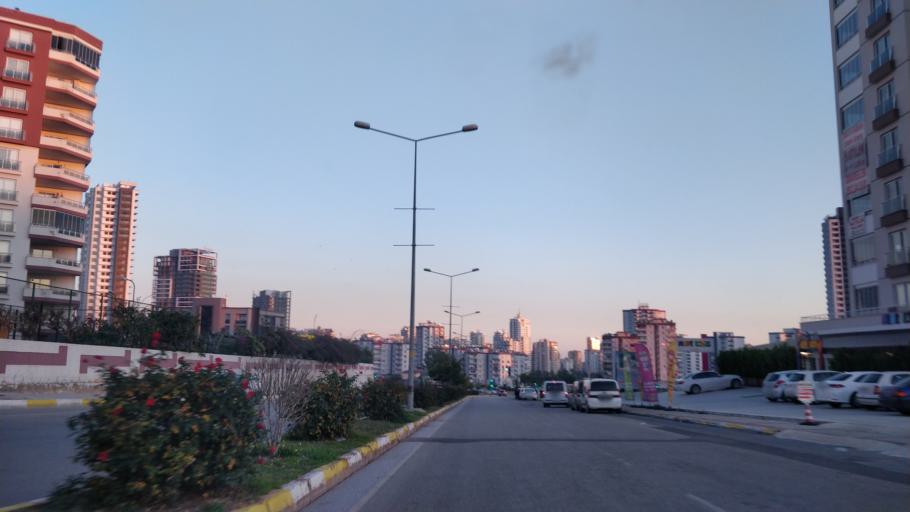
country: TR
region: Mersin
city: Mercin
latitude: 36.7986
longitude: 34.5758
